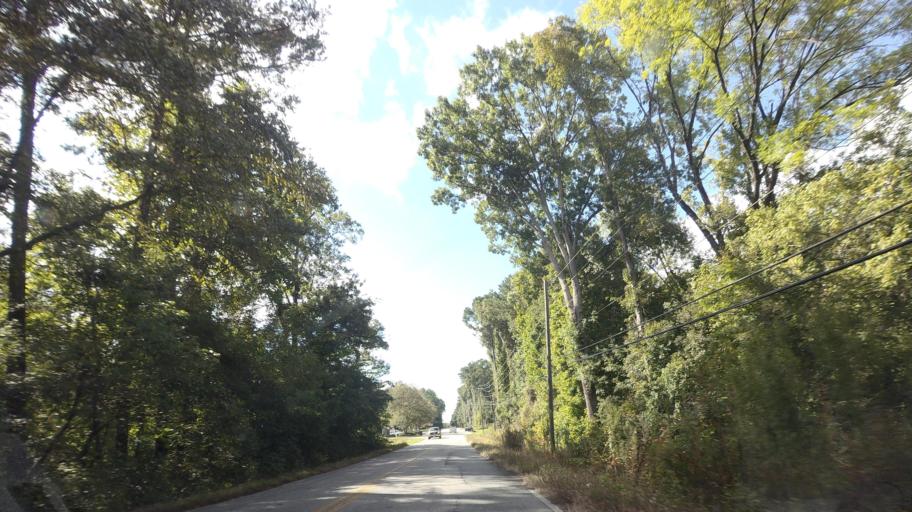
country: US
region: Georgia
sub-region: Bibb County
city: Macon
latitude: 32.9110
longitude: -83.6901
